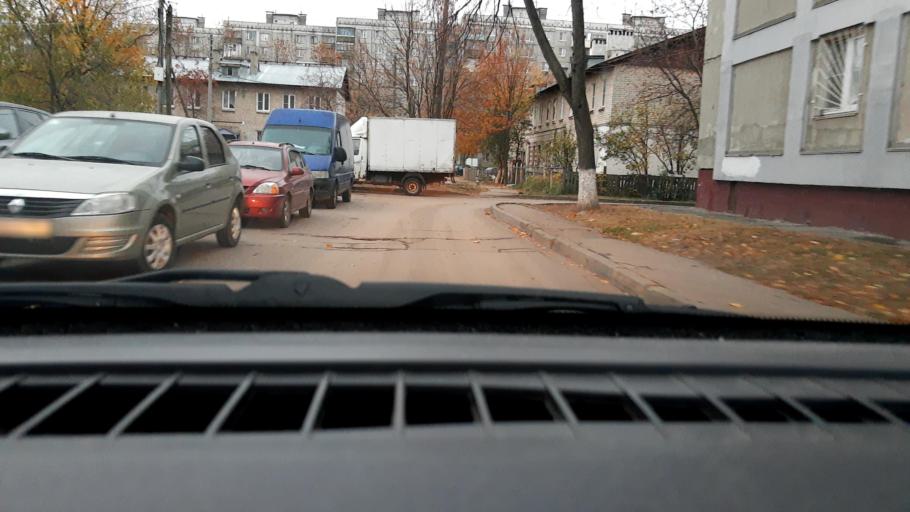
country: RU
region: Nizjnij Novgorod
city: Gorbatovka
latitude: 56.2547
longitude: 43.8455
